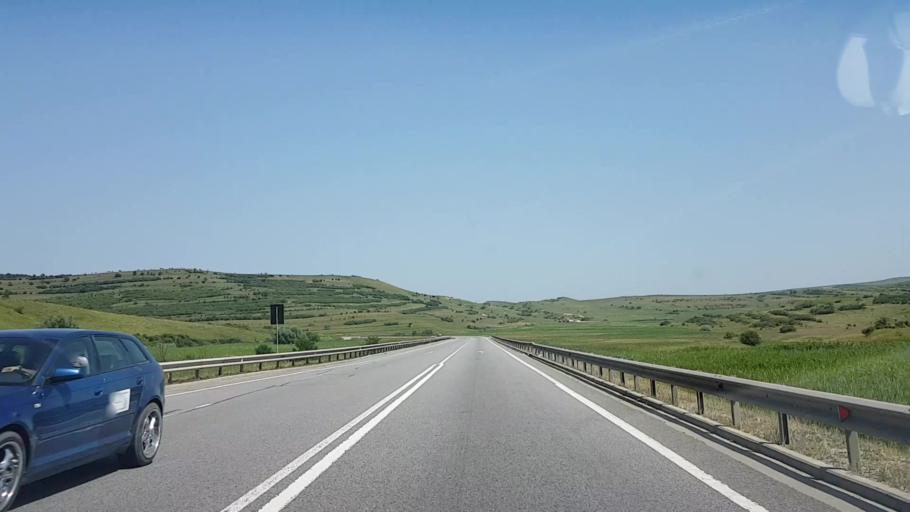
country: RO
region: Cluj
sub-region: Comuna Feleacu
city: Gheorghieni
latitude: 46.7327
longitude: 23.6975
